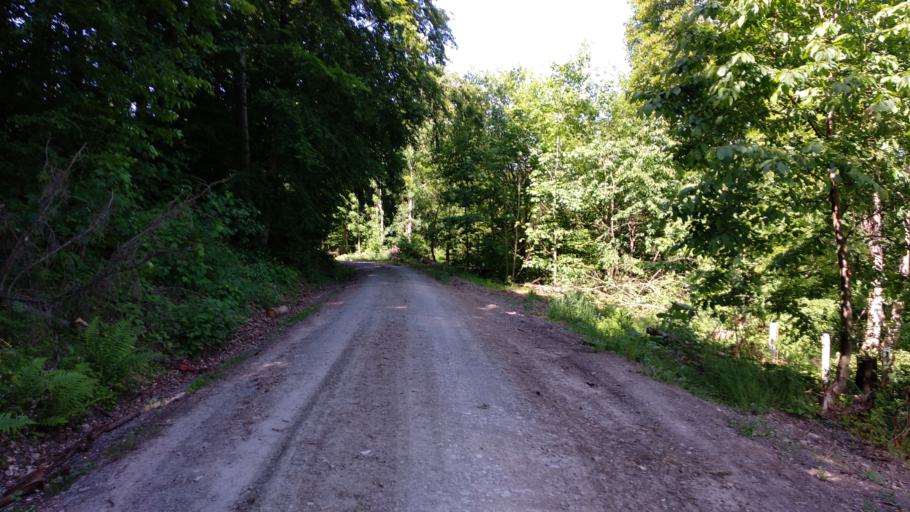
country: DE
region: North Rhine-Westphalia
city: Beverungen
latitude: 51.6475
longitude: 9.3513
